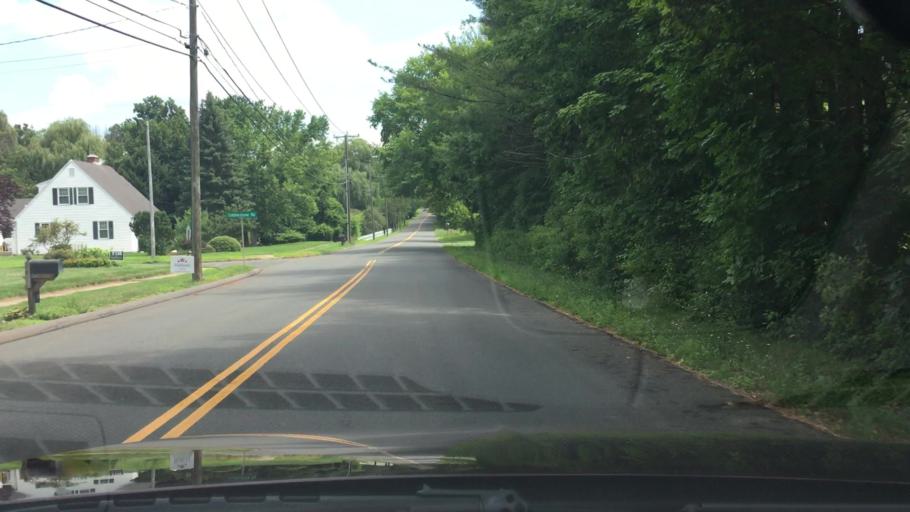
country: US
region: Connecticut
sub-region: Hartford County
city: Kensington
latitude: 41.6349
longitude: -72.7324
